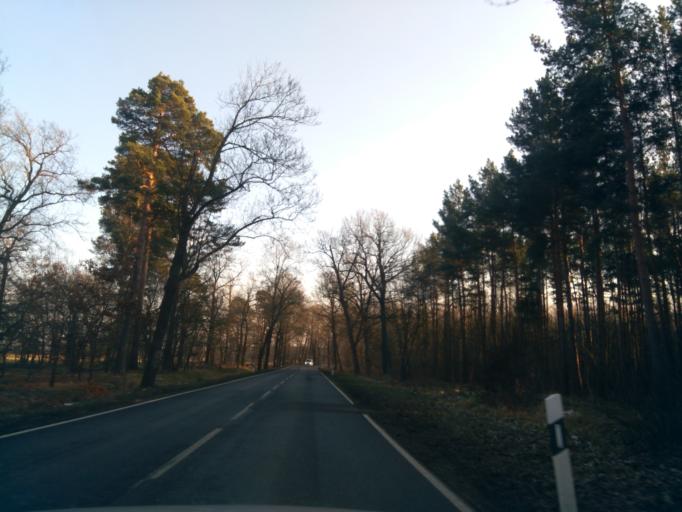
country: DE
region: Brandenburg
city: Brieselang
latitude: 52.5996
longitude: 13.0454
